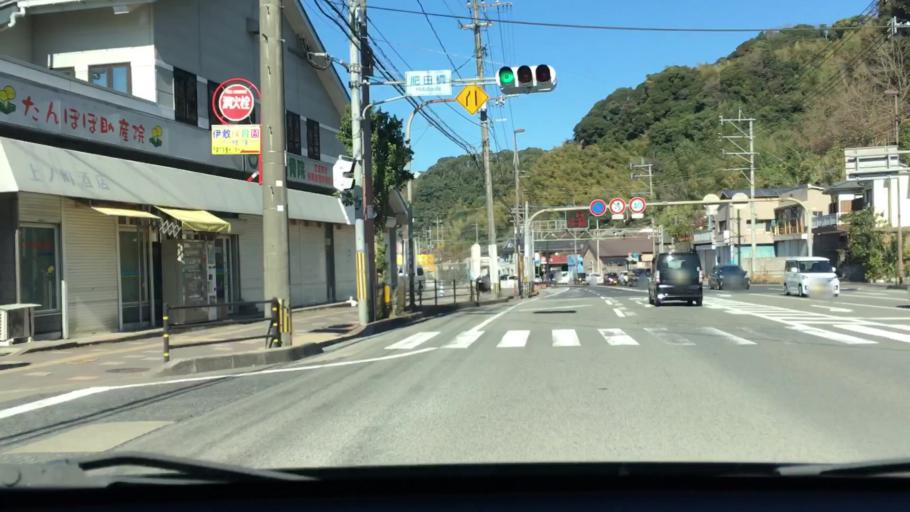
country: JP
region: Kagoshima
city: Kagoshima-shi
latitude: 31.6282
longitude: 130.5250
